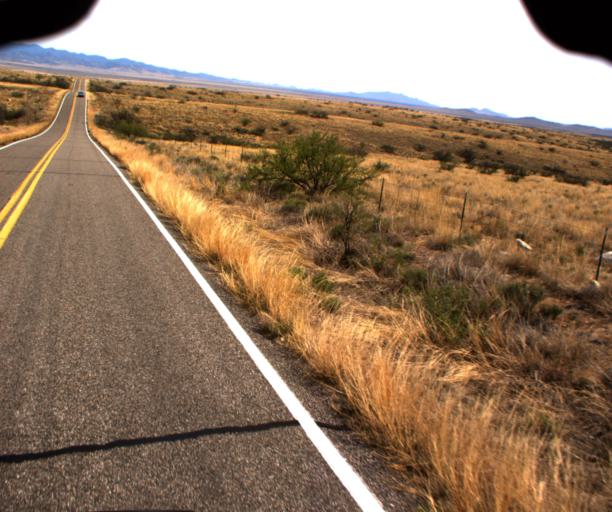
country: US
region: Arizona
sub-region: Cochise County
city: Willcox
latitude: 32.1396
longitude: -109.5641
